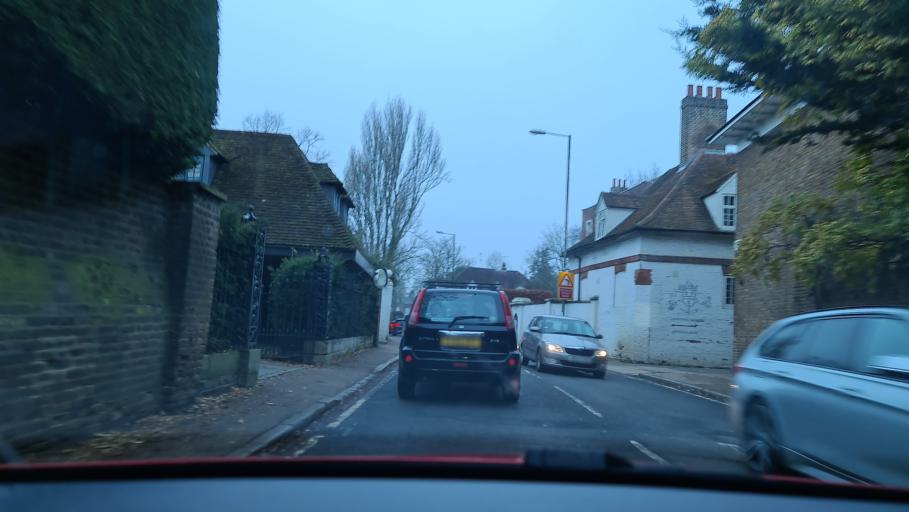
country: GB
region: England
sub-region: Greater London
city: Richmond
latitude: 51.4463
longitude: -0.3010
